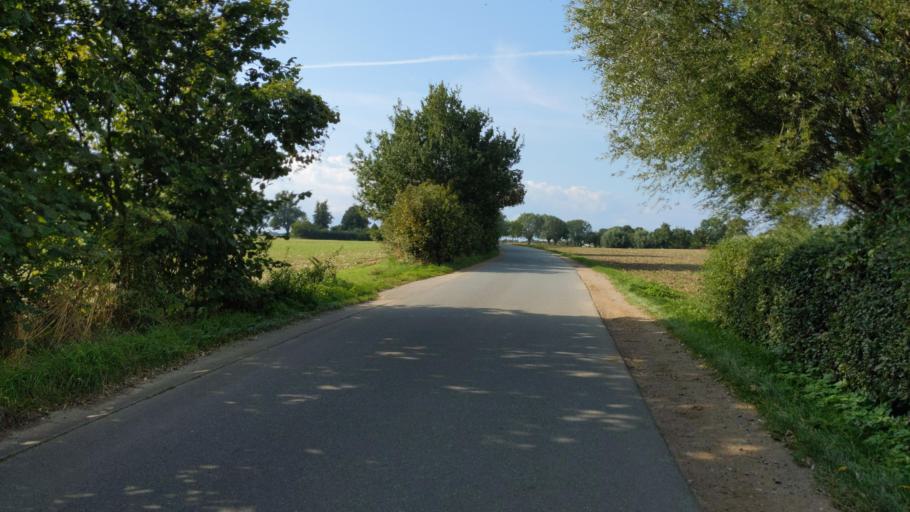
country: DE
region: Mecklenburg-Vorpommern
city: Kalkhorst
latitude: 53.9759
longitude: 11.0095
